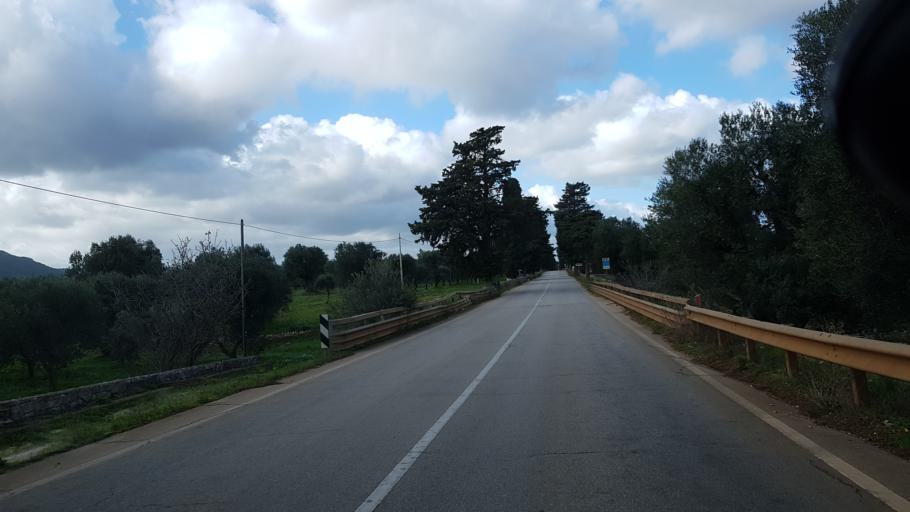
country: IT
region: Apulia
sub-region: Provincia di Brindisi
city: Montalbano
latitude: 40.7634
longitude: 17.5227
